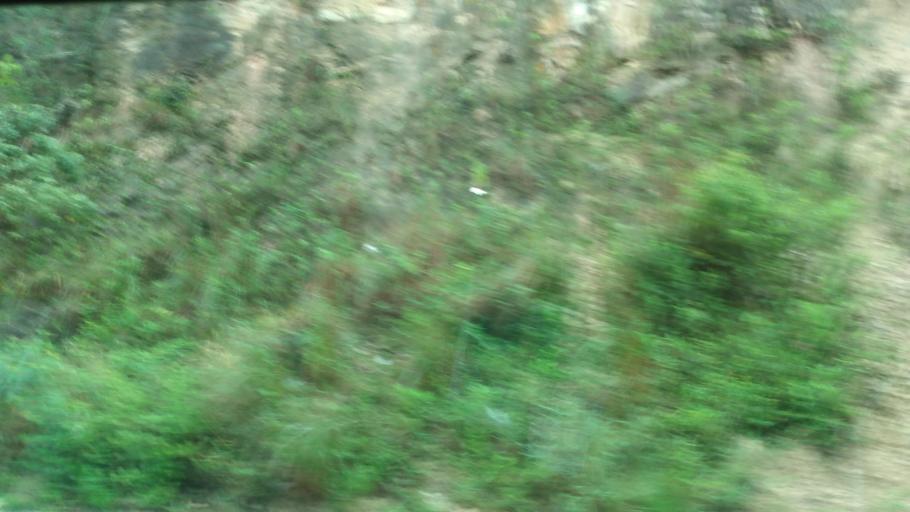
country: BR
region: Pernambuco
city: Garanhuns
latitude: -8.8779
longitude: -36.5117
